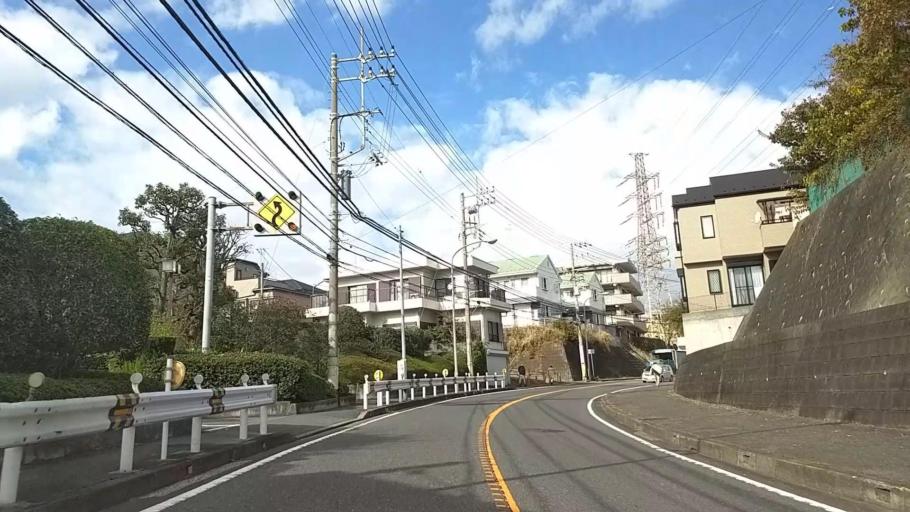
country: JP
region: Kanagawa
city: Yokohama
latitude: 35.4926
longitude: 139.6356
